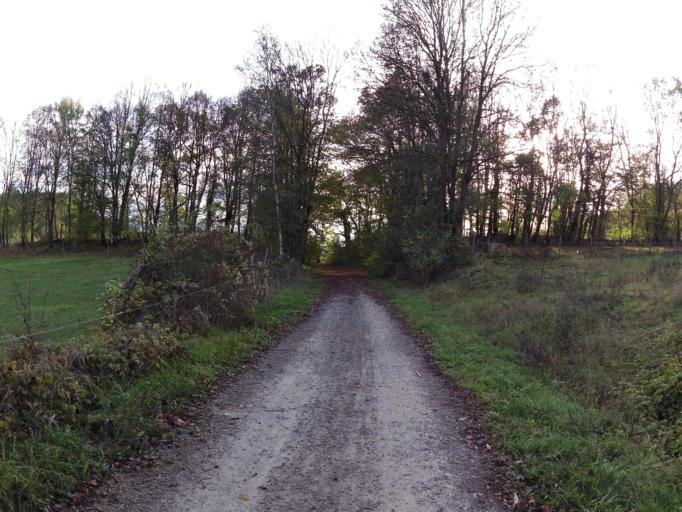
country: DE
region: Thuringia
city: Creuzburg
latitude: 51.0588
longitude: 10.2513
